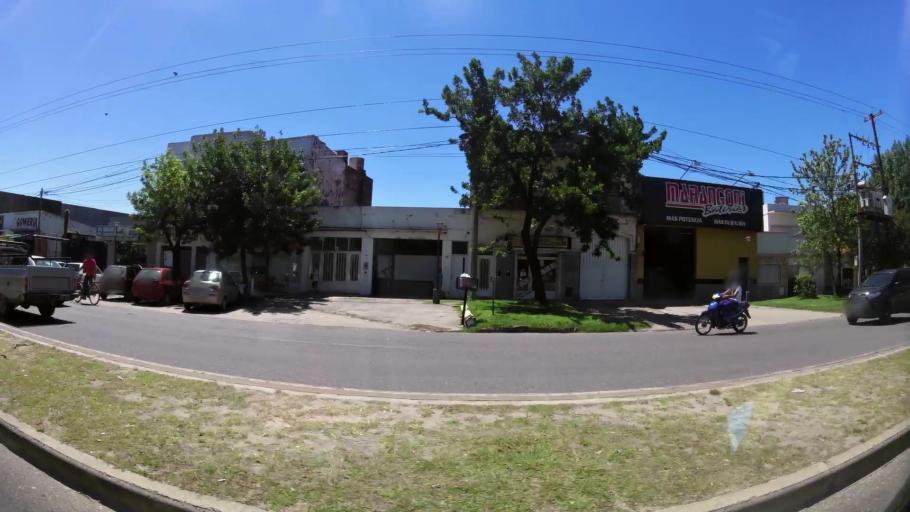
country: AR
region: Santa Fe
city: Santa Fe de la Vera Cruz
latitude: -31.6236
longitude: -60.7135
